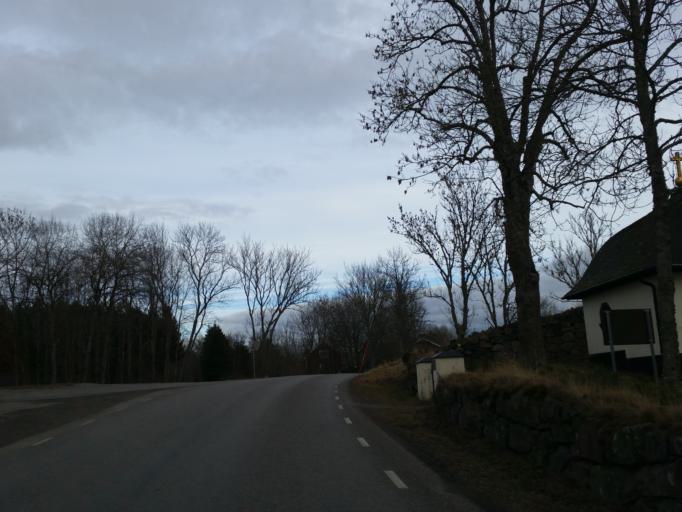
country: SE
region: OEstergoetland
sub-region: Soderkopings Kommun
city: Soederkoeping
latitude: 58.5295
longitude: 16.2917
